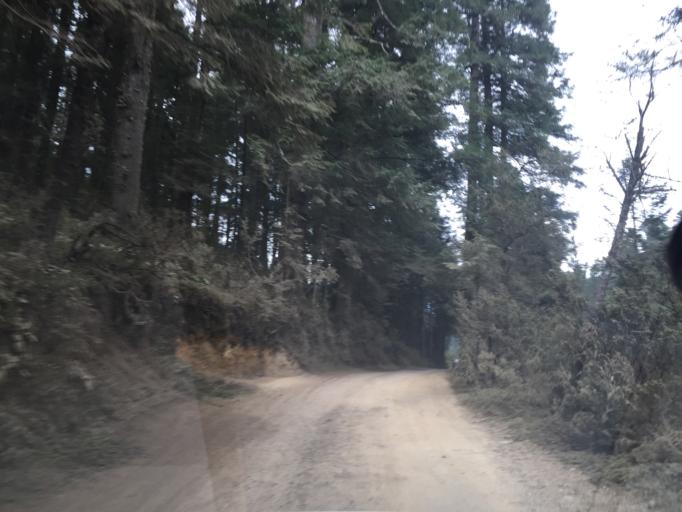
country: MX
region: Michoacan
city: Mineral de Angangueo
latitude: 19.6640
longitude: -100.2733
